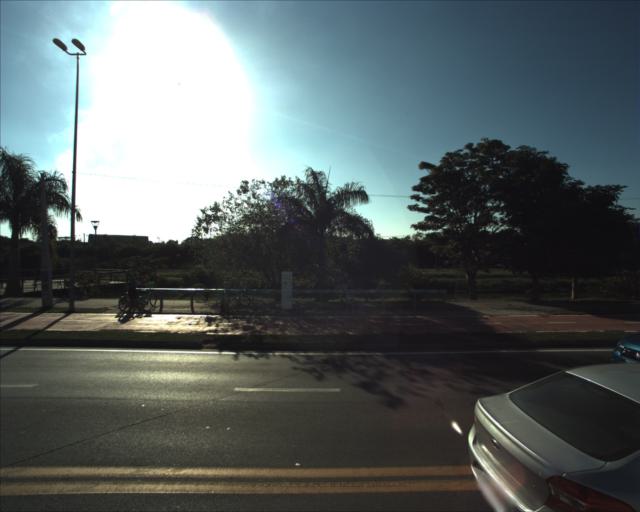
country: BR
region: Sao Paulo
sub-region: Sorocaba
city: Sorocaba
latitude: -23.4693
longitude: -47.4474
